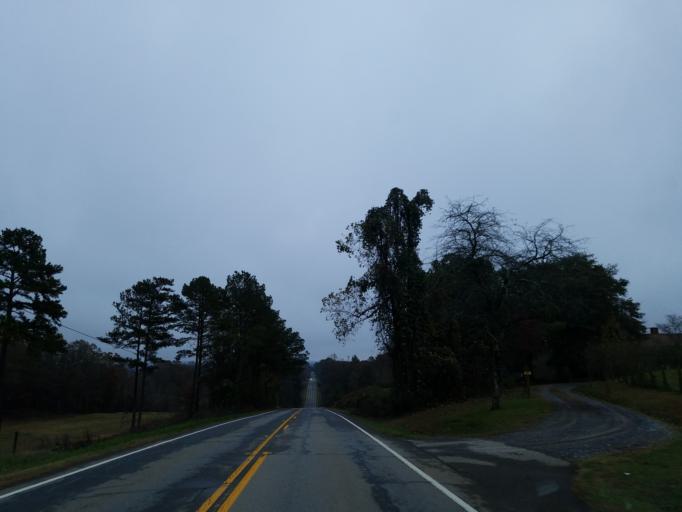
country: US
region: Georgia
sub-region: Pickens County
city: Jasper
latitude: 34.3923
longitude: -84.4614
